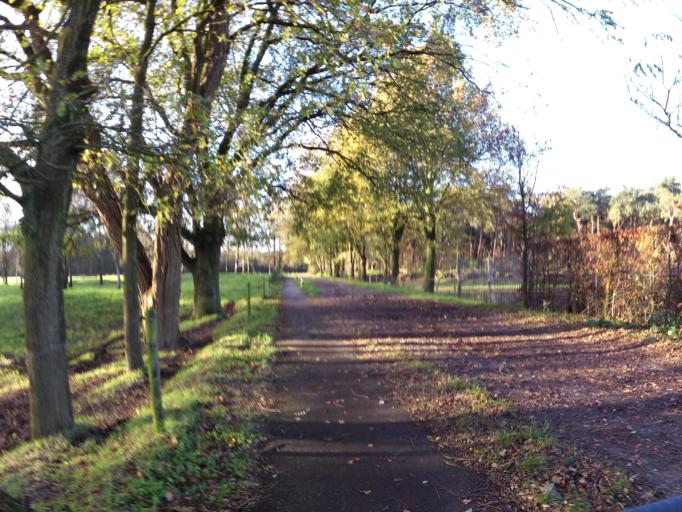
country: NL
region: North Brabant
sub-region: Gemeente Haaren
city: Haaren
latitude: 51.6481
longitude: 5.2175
